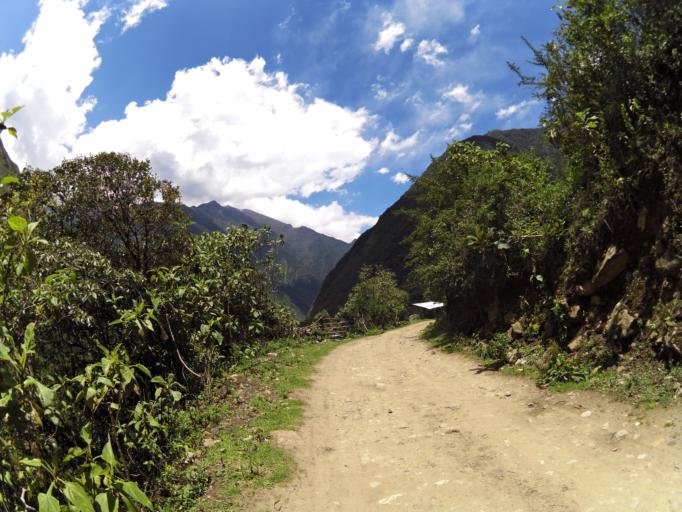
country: PE
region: Cusco
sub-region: Provincia de La Convencion
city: Santa Teresa
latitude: -13.3259
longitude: -72.6650
